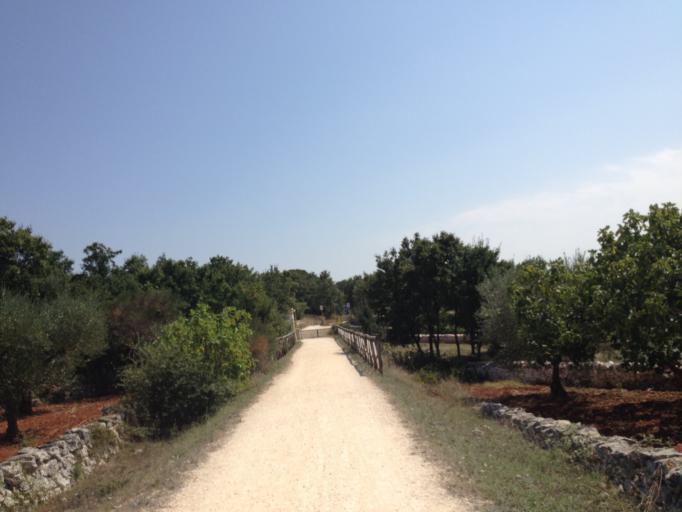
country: IT
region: Apulia
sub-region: Provincia di Brindisi
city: Cisternino
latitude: 40.7096
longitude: 17.4110
